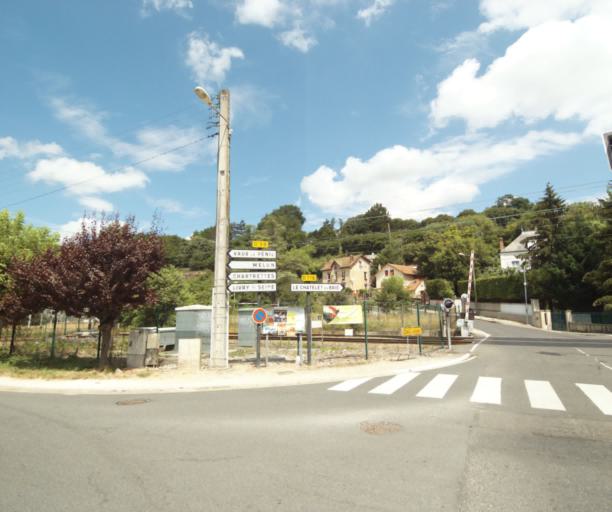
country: FR
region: Ile-de-France
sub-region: Departement de Seine-et-Marne
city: Samois-sur-Seine
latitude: 48.4866
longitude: 2.7526
